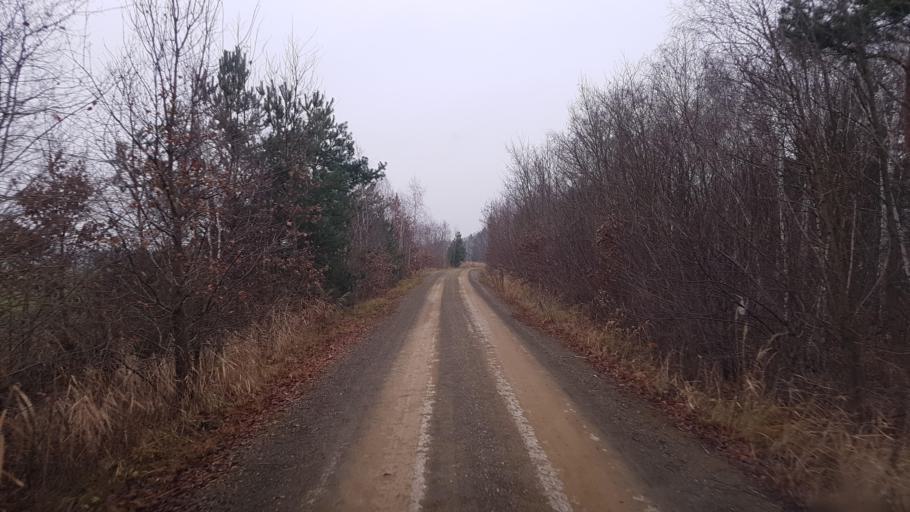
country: DE
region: Brandenburg
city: Plessa
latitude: 51.5088
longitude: 13.6585
